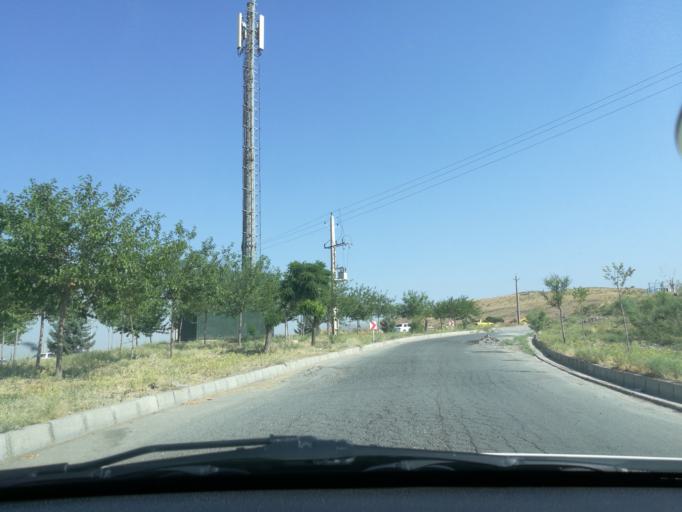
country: IR
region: Alborz
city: Karaj
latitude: 35.8654
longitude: 50.9278
